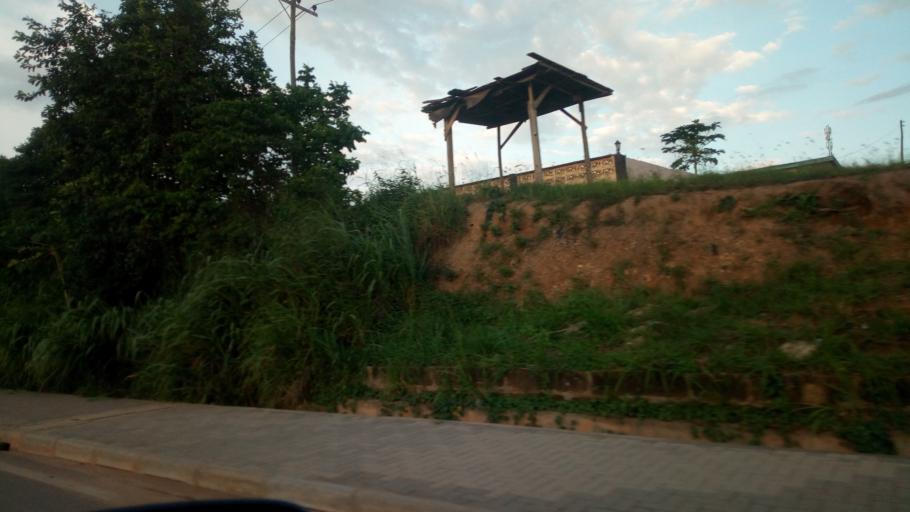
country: GH
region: Western
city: Takoradi
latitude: 4.9383
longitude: -1.7772
